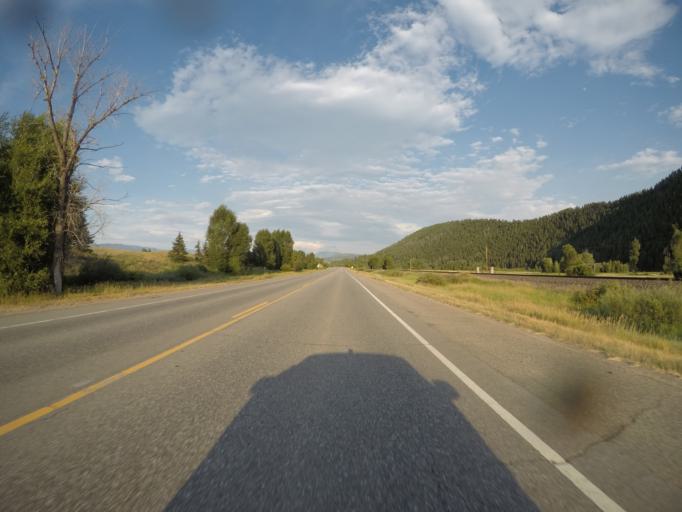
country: US
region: Colorado
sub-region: Routt County
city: Steamboat Springs
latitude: 40.4849
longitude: -106.9866
